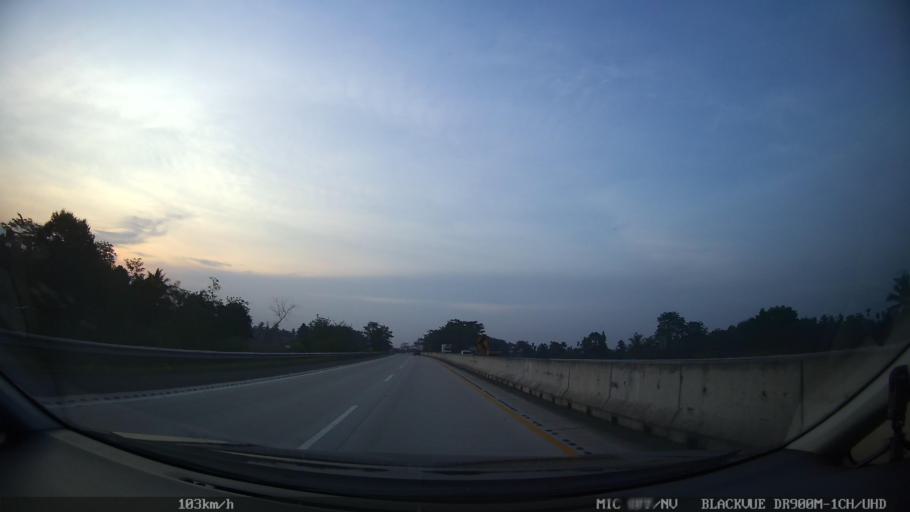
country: ID
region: Lampung
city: Penengahan
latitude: -5.7497
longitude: 105.7058
